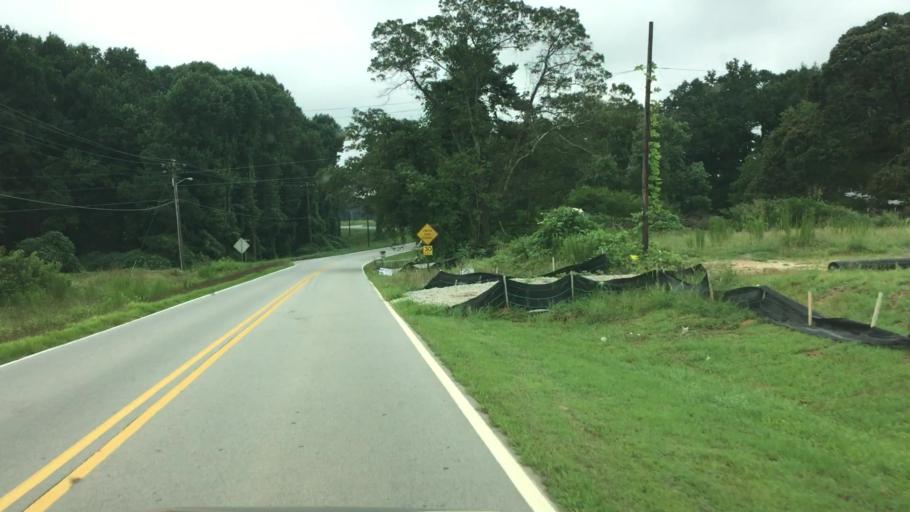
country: US
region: Georgia
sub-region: Barrow County
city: Winder
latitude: 34.0248
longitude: -83.7545
